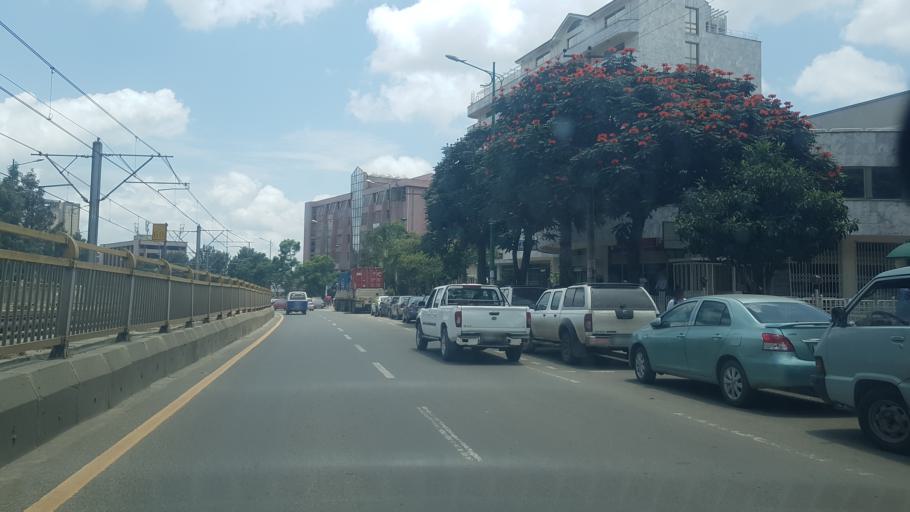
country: ET
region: Adis Abeba
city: Addis Ababa
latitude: 8.9930
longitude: 38.7593
